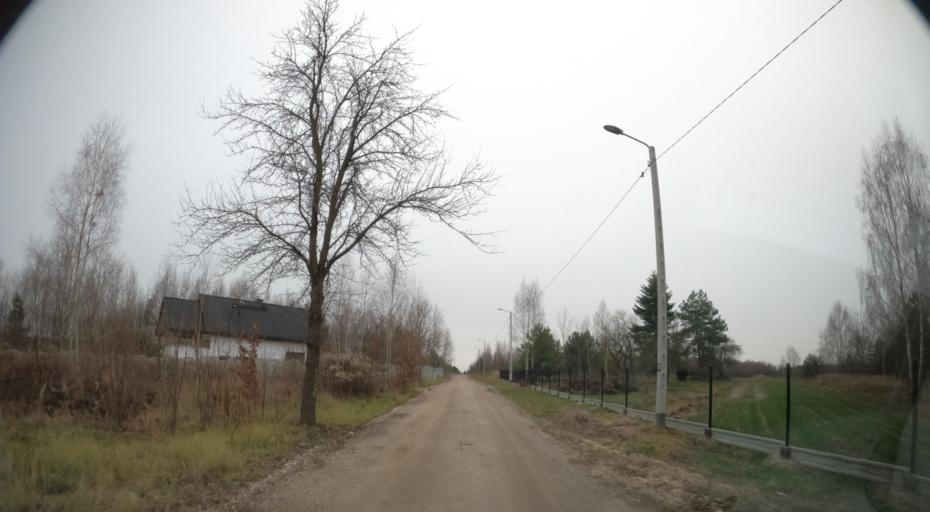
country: PL
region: Masovian Voivodeship
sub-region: Powiat radomski
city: Jastrzebia
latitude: 51.4831
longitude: 21.1914
